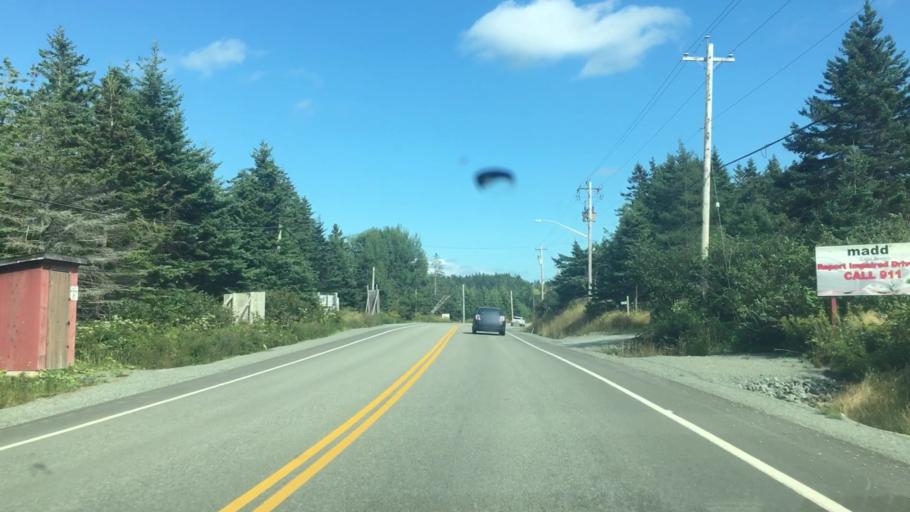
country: CA
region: Nova Scotia
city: Princeville
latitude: 45.6505
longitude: -60.8512
